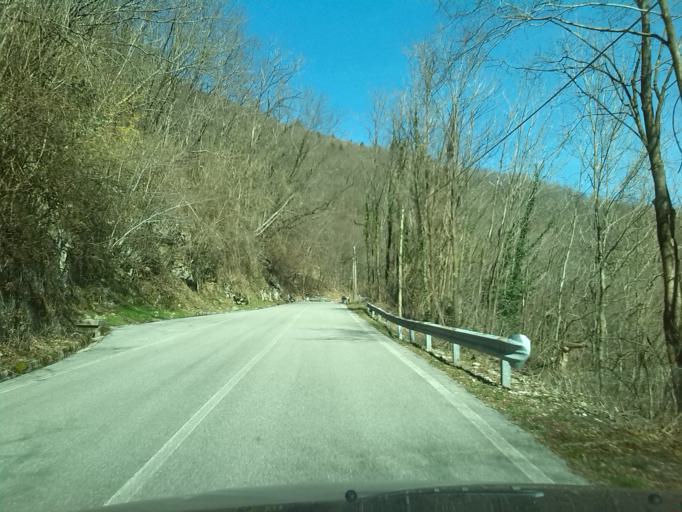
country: IT
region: Friuli Venezia Giulia
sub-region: Provincia di Udine
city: Savogna
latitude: 46.1697
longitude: 13.5576
